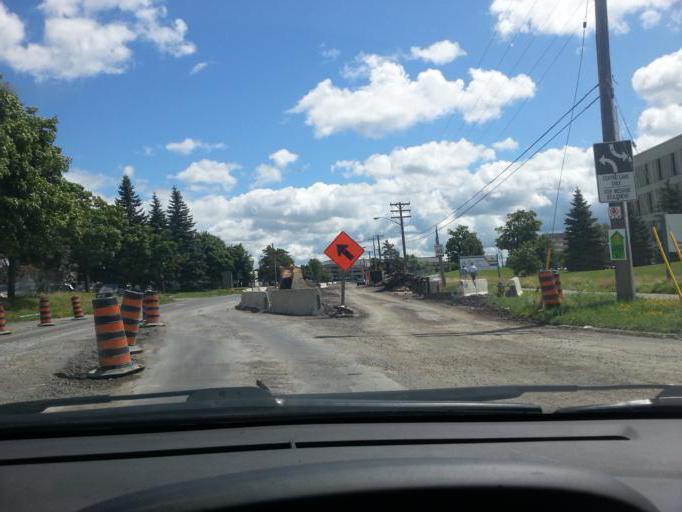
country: CA
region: Ontario
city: Ottawa
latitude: 45.4215
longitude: -75.6470
